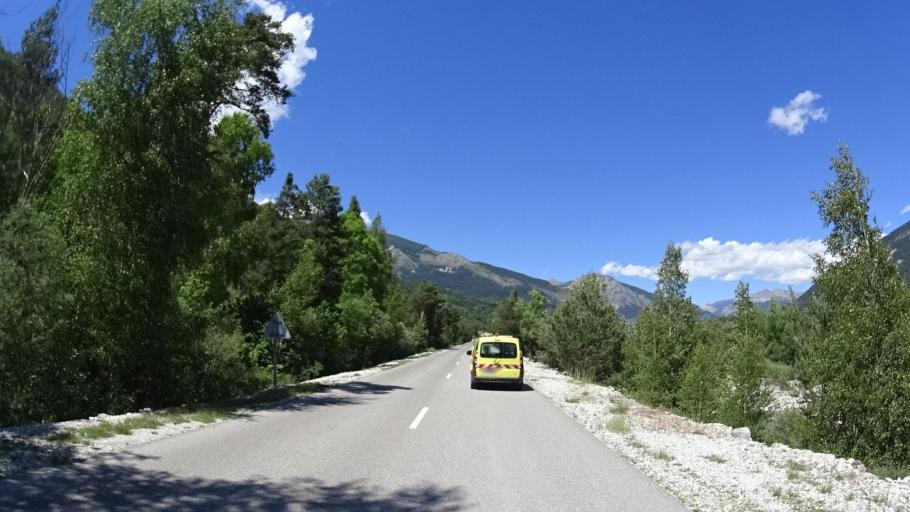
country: FR
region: Provence-Alpes-Cote d'Azur
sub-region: Departement des Alpes-de-Haute-Provence
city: Annot
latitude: 44.1224
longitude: 6.5805
